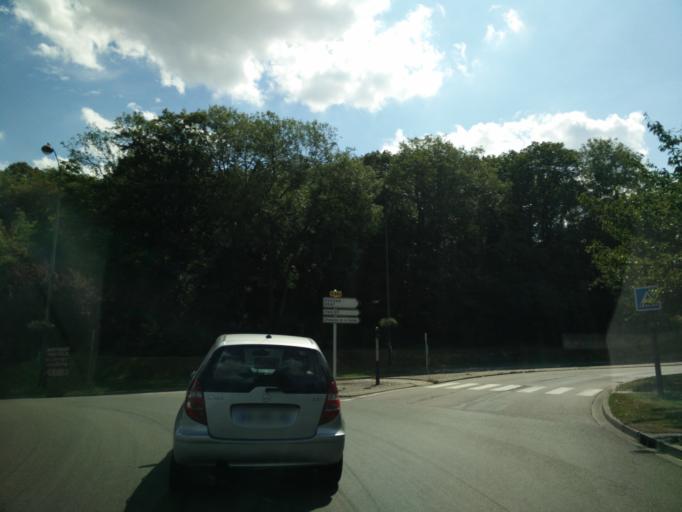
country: FR
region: Ile-de-France
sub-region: Departement des Yvelines
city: Mantes-la-Jolie
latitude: 48.9754
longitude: 1.7175
